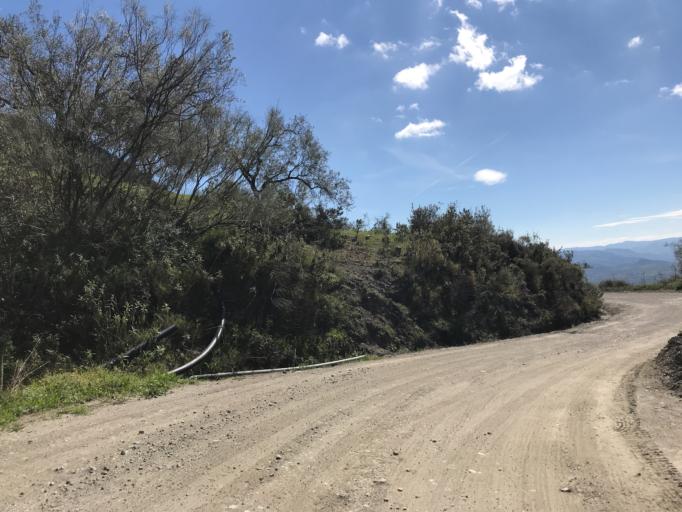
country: ES
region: Andalusia
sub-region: Provincia de Malaga
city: Alcaucin
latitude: 36.9153
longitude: -4.1024
